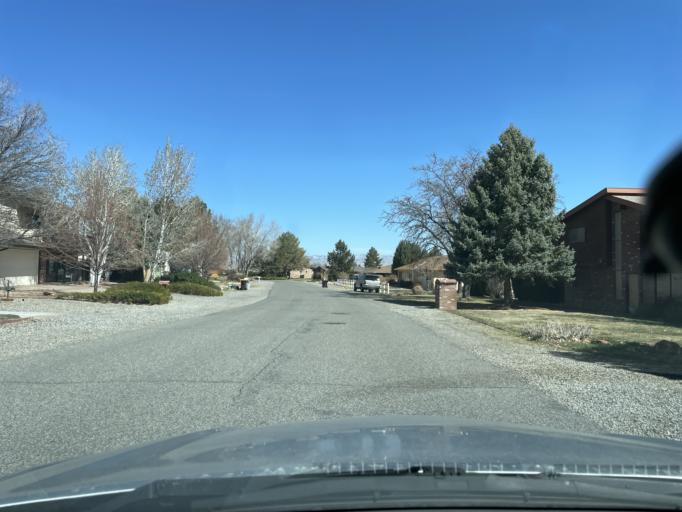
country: US
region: Colorado
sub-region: Mesa County
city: Redlands
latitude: 39.0824
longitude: -108.6718
